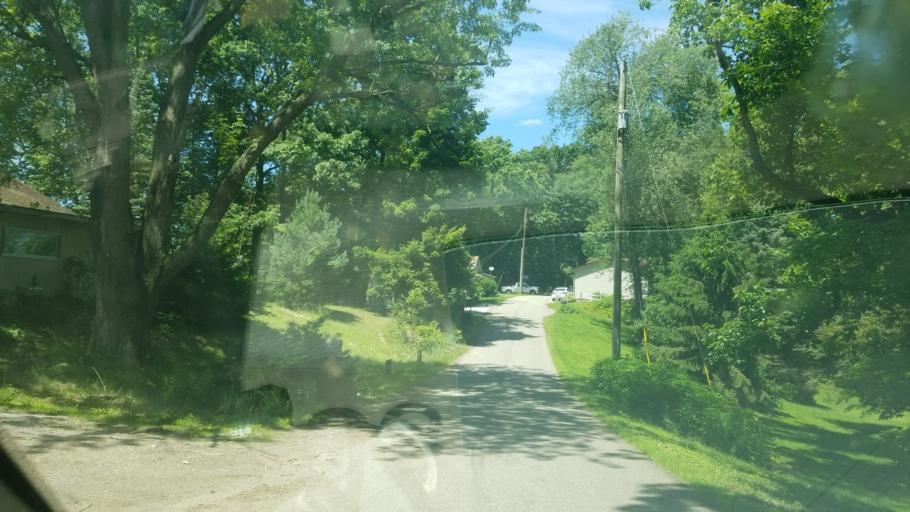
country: US
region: Ohio
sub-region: Mahoning County
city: Sebring
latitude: 40.8514
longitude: -80.9916
